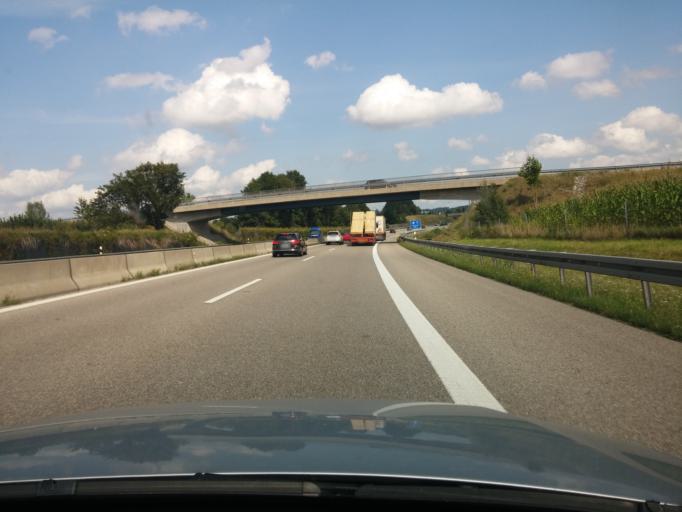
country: DE
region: Bavaria
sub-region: Swabia
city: Holzgunz
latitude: 48.0169
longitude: 10.2577
